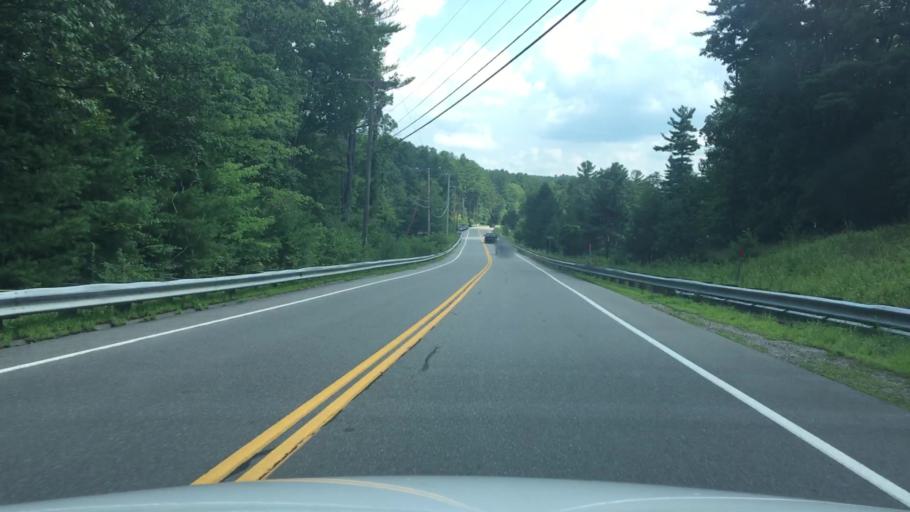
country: US
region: New Hampshire
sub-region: Rockingham County
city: Auburn
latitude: 42.9895
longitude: -71.3772
